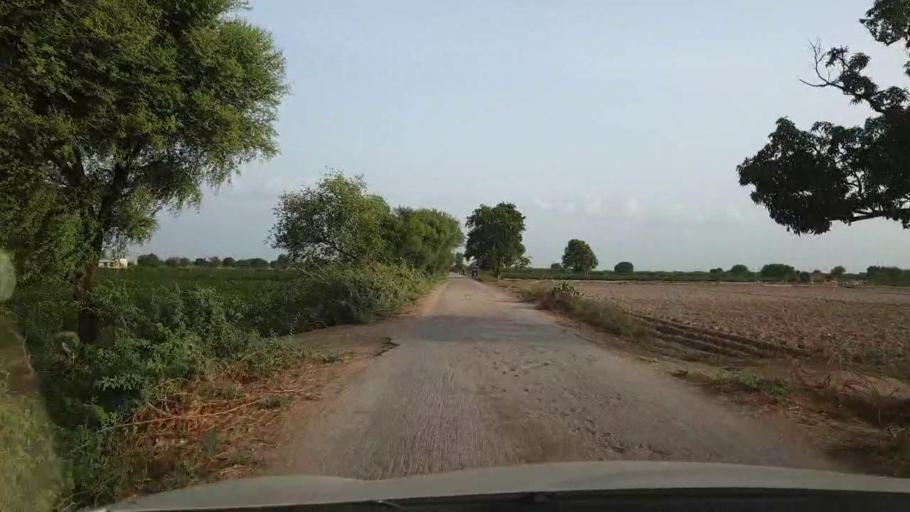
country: PK
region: Sindh
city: Tando Ghulam Ali
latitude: 25.1068
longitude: 68.8849
